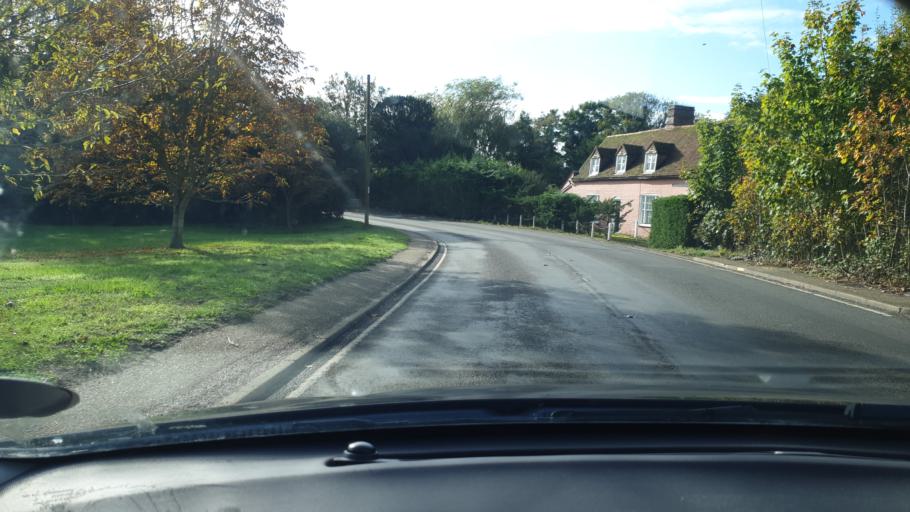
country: GB
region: England
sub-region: Essex
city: Alresford
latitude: 51.8940
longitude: 1.0271
